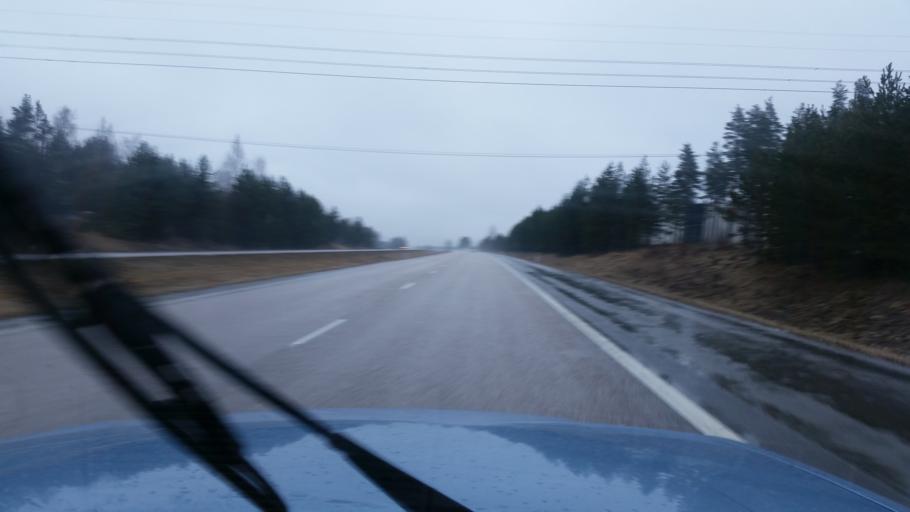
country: FI
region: Uusimaa
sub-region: Helsinki
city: Nurmijaervi
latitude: 60.4902
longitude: 24.8514
